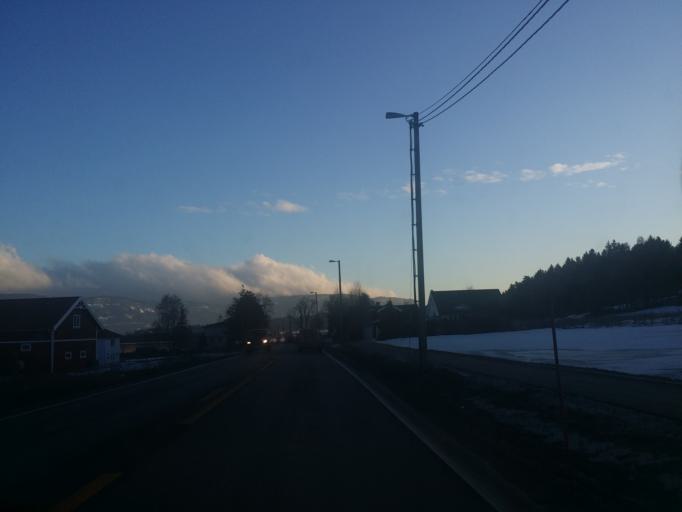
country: NO
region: Buskerud
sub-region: Hole
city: Vik
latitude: 60.1189
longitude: 10.2814
